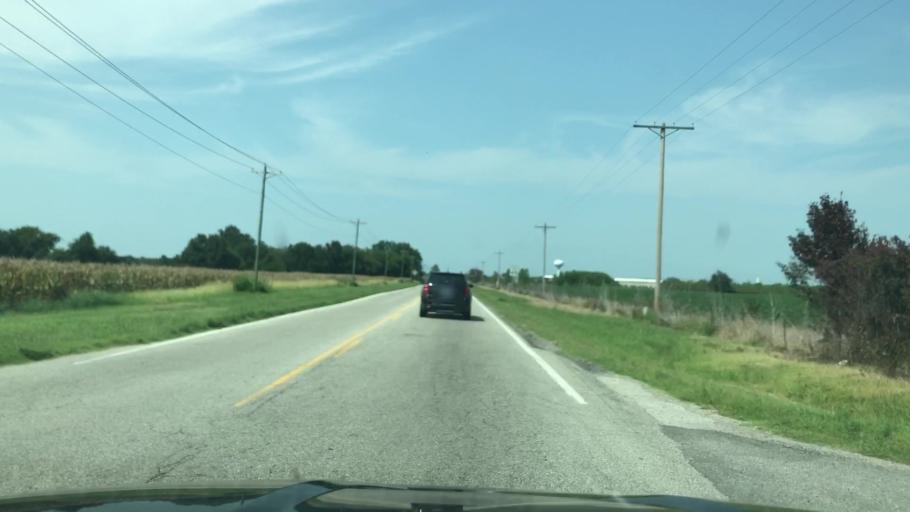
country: US
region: Oklahoma
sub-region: Ottawa County
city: Miami
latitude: 36.9002
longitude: -94.8419
